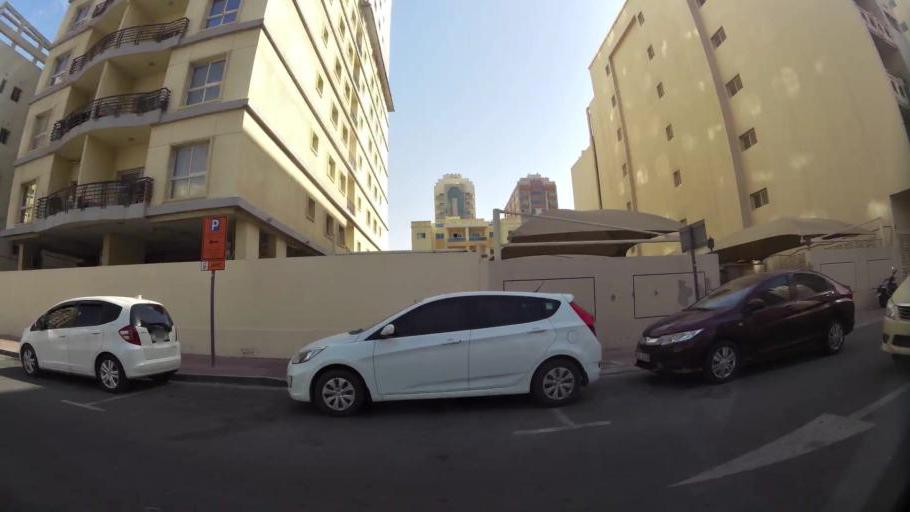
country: AE
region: Ash Shariqah
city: Sharjah
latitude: 25.2935
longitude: 55.3797
